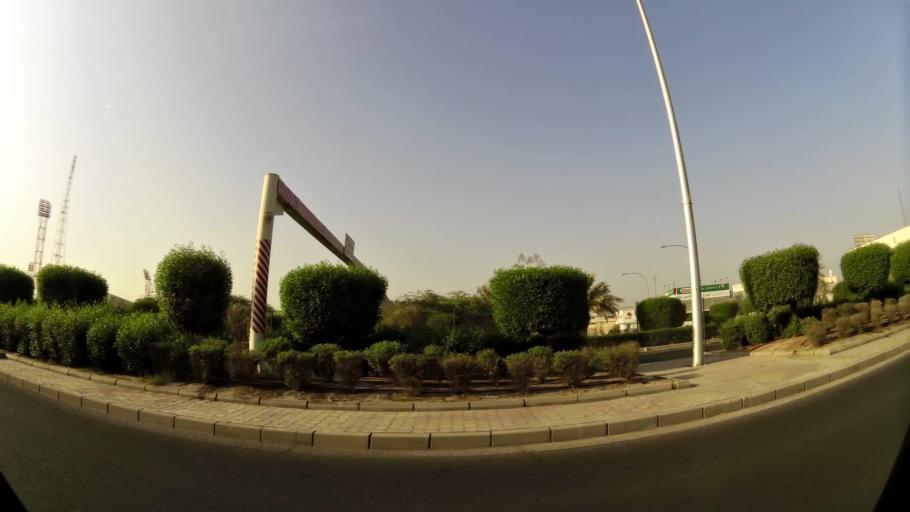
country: KW
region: Al Asimah
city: Ad Dasmah
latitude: 29.3601
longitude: 47.9990
